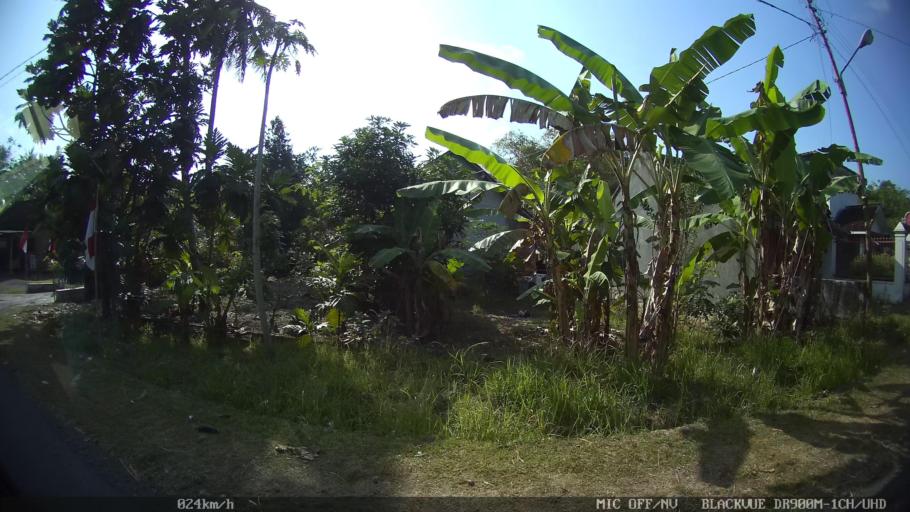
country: ID
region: Daerah Istimewa Yogyakarta
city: Gamping Lor
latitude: -7.8126
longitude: 110.2992
